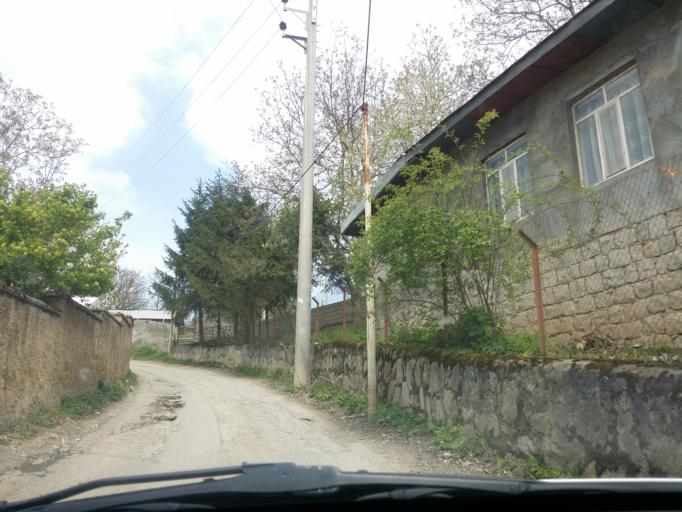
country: IR
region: Mazandaran
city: `Abbasabad
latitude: 36.4895
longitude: 51.1510
